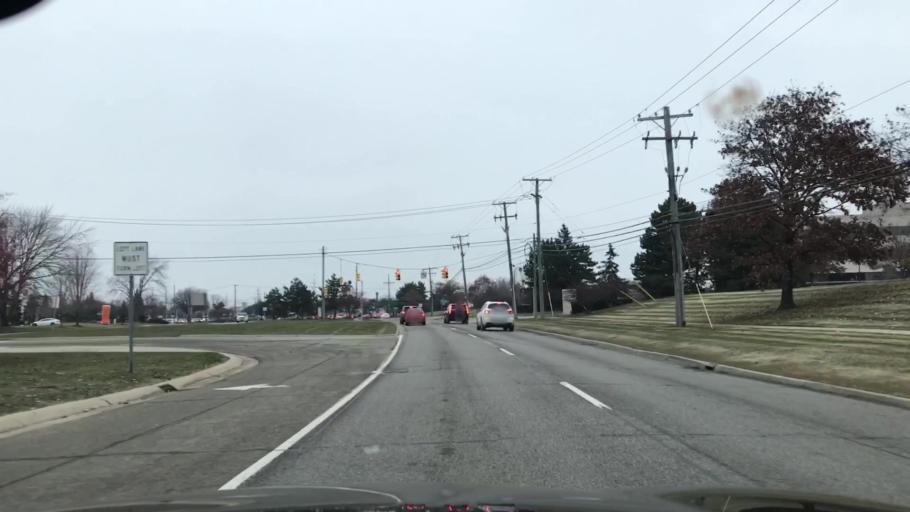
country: US
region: Michigan
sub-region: Oakland County
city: Clawson
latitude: 42.5464
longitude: -83.1204
